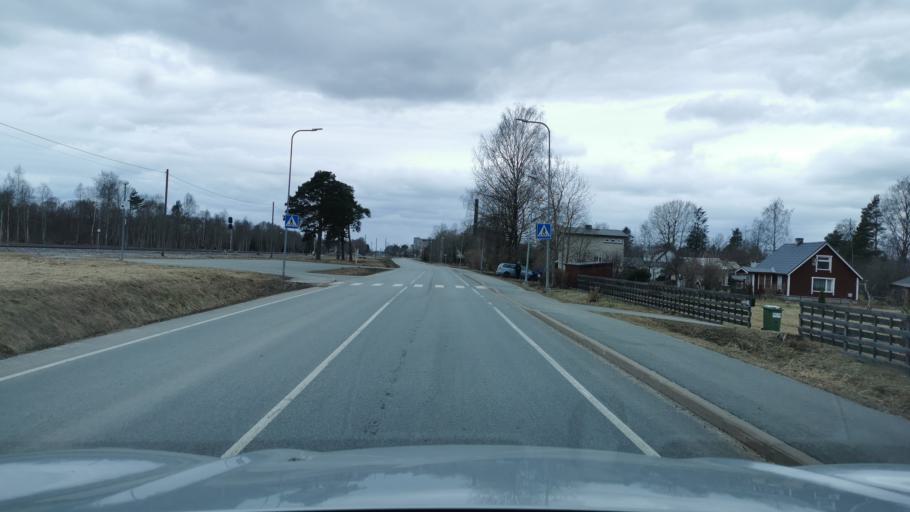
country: EE
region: Ida-Virumaa
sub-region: Puessi linn
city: Pussi
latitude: 59.3589
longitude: 27.0489
